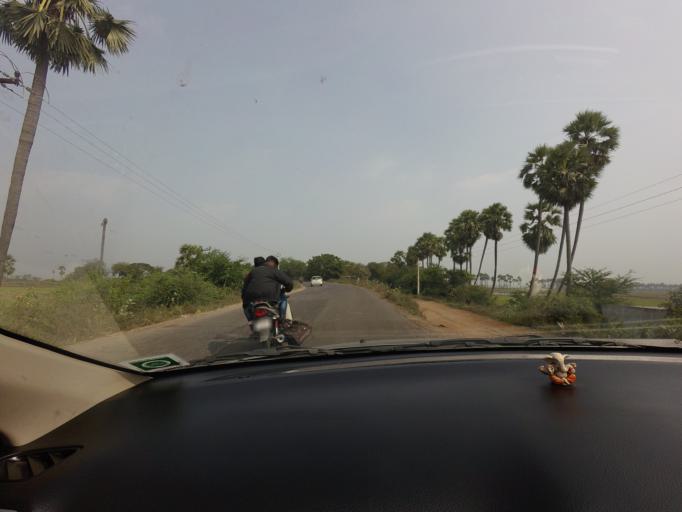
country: IN
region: Andhra Pradesh
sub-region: Krishna
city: Kankipadu
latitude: 16.4543
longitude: 80.7932
